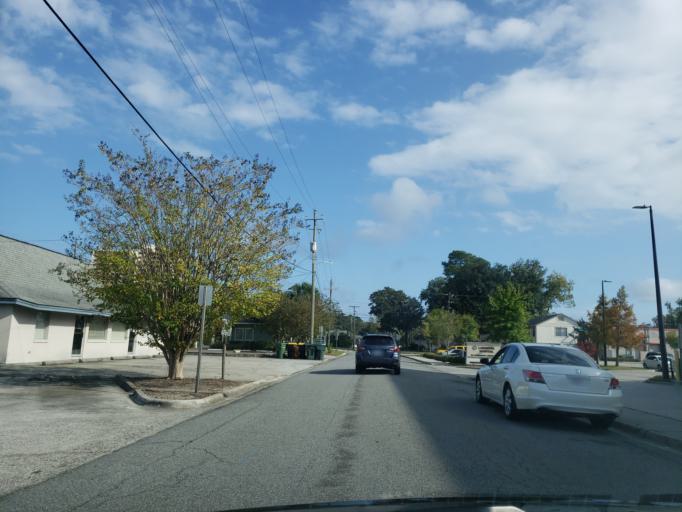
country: US
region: Georgia
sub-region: Chatham County
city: Thunderbolt
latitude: 32.0290
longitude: -81.0951
